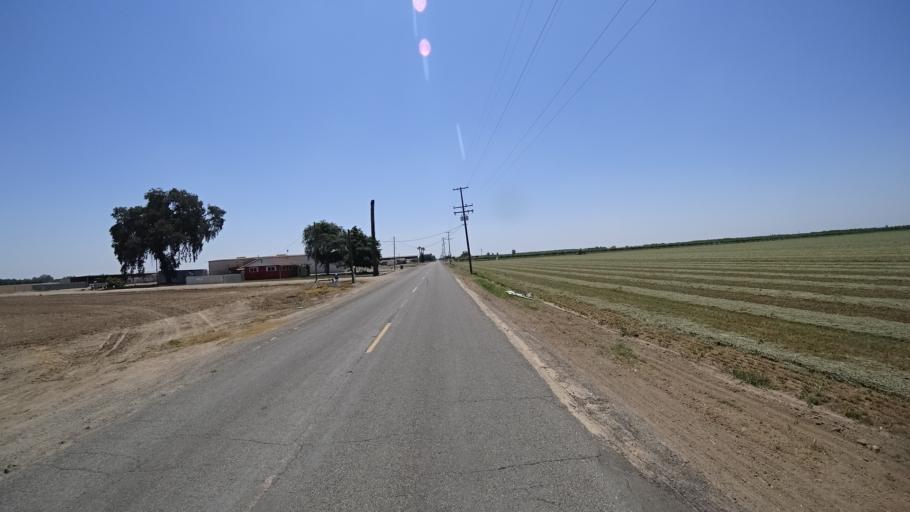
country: US
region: California
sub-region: Kings County
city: Armona
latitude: 36.3557
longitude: -119.7269
